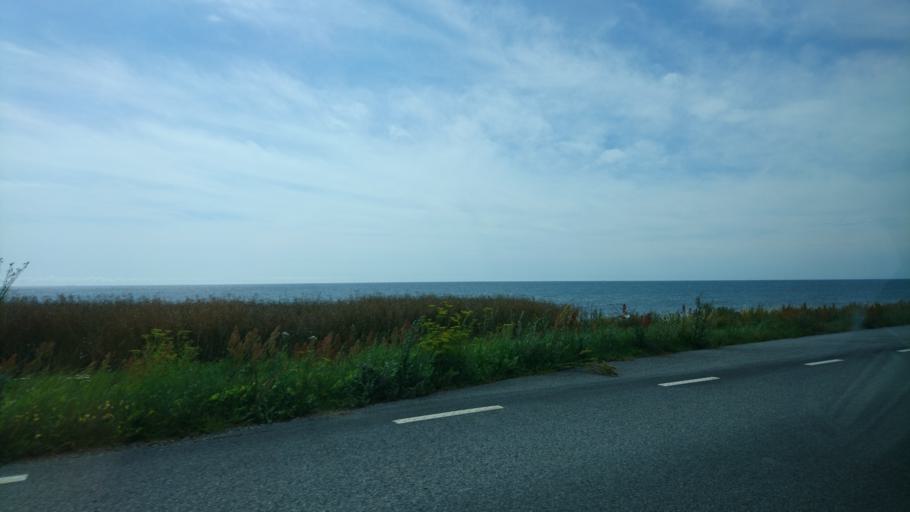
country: SE
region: Skane
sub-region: Skurups Kommun
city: Skivarp
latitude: 55.3855
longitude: 13.5610
